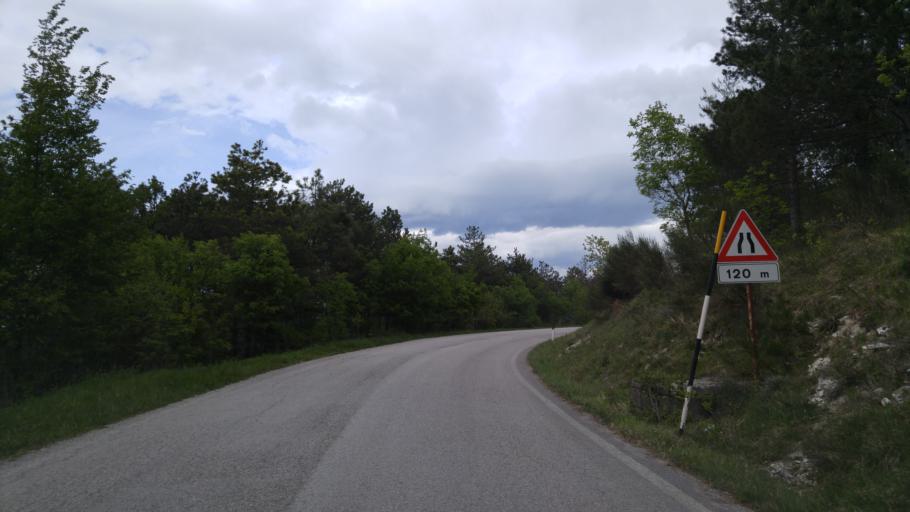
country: IT
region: The Marches
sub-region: Provincia di Pesaro e Urbino
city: Canavaccio
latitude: 43.7158
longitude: 12.7271
